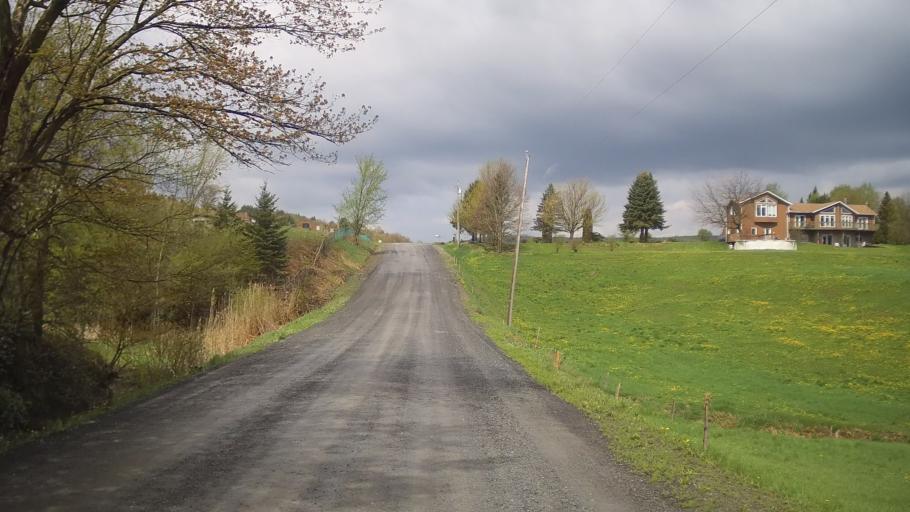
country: CA
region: Quebec
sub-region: Monteregie
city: Cowansville
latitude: 45.1738
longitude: -72.6757
